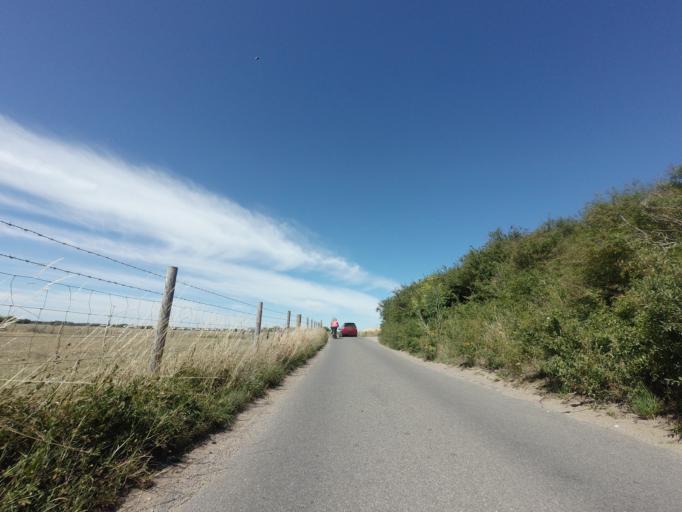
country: GB
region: England
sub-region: Kent
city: Deal
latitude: 51.2465
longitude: 1.3951
